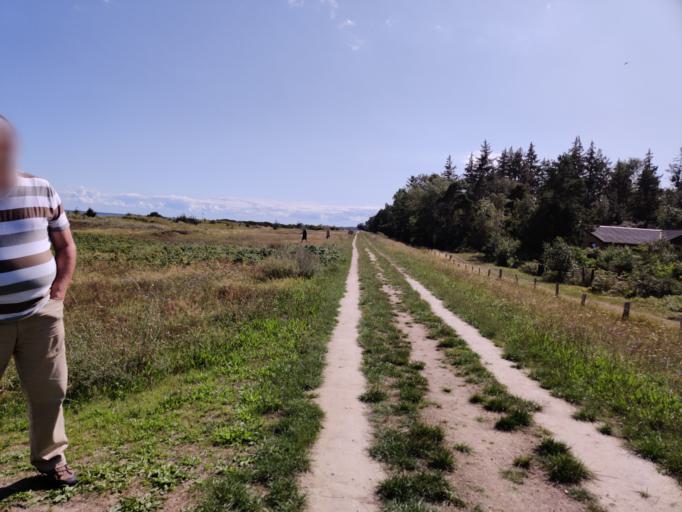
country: DK
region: Zealand
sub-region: Guldborgsund Kommune
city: Nykobing Falster
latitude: 54.6467
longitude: 11.9601
